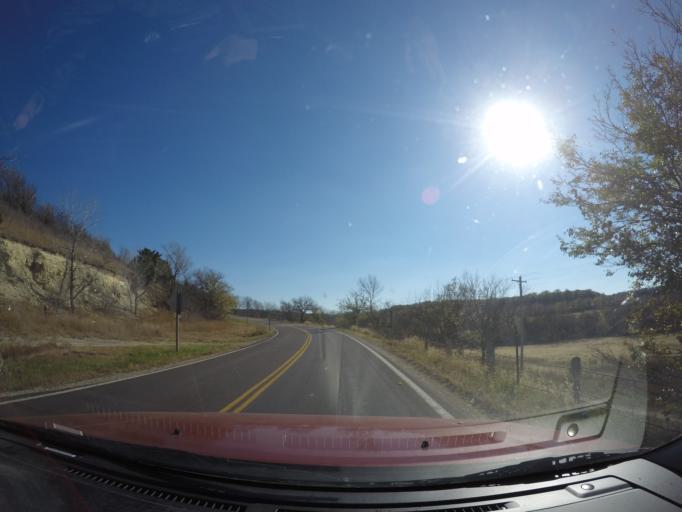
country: US
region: Kansas
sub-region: Geary County
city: Grandview Plaza
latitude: 39.0280
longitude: -96.7818
